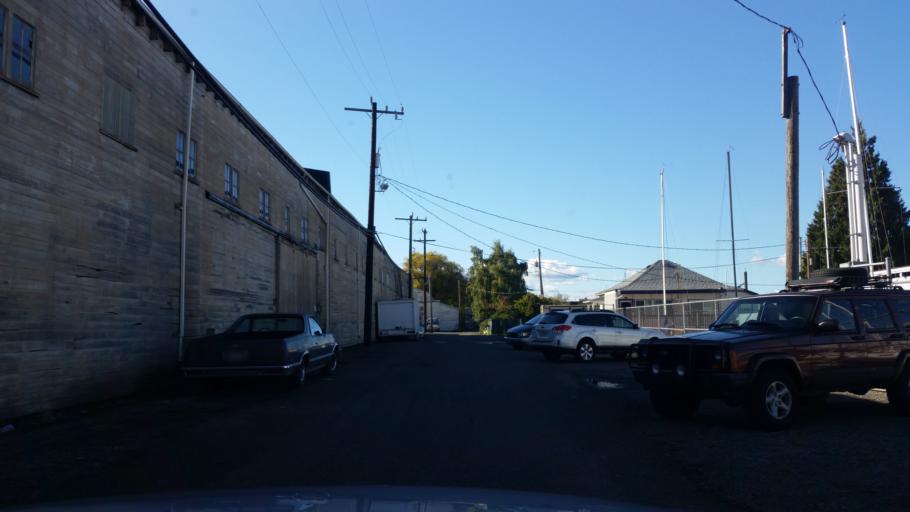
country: US
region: Washington
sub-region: King County
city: Seattle
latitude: 47.6523
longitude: -122.3626
